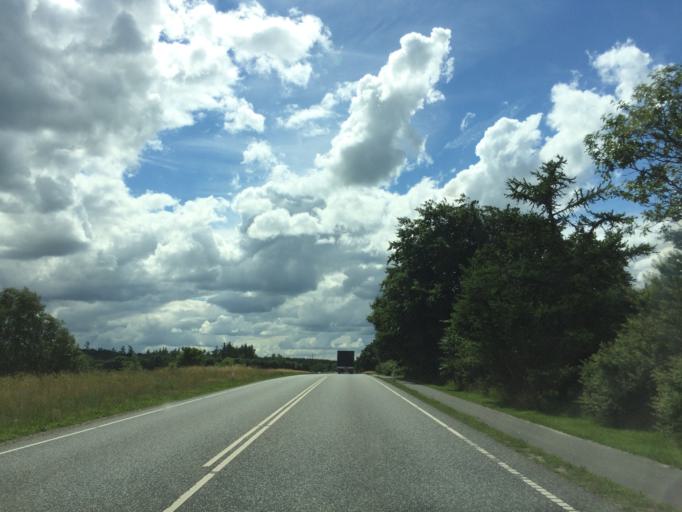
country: DK
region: North Denmark
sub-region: Vesthimmerland Kommune
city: Alestrup
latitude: 56.5704
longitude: 9.4890
